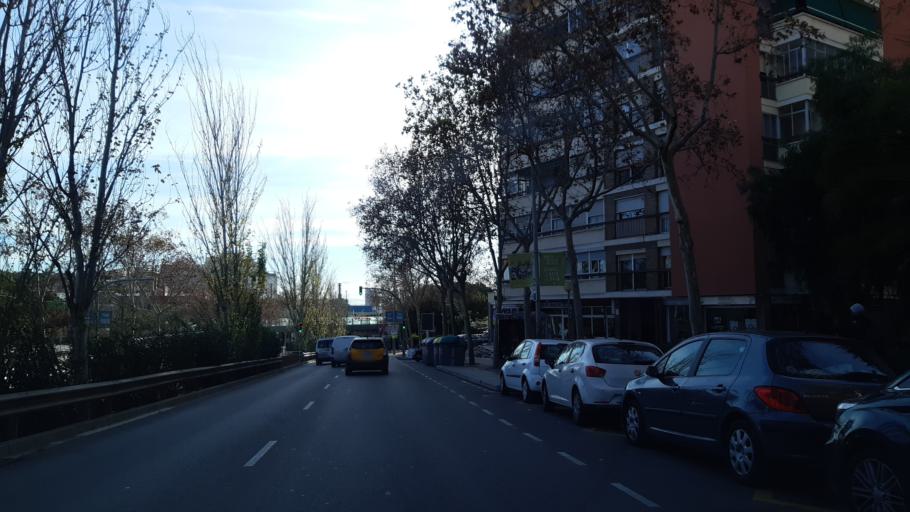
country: ES
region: Catalonia
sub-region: Provincia de Barcelona
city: L'Hospitalet de Llobregat
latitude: 41.3667
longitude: 2.1037
